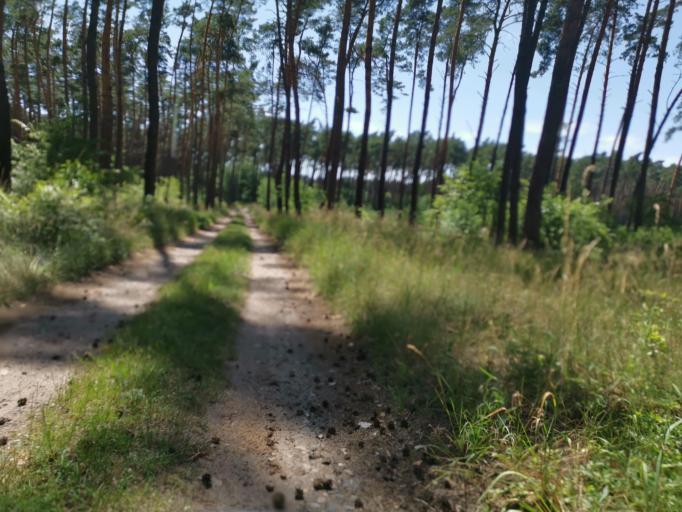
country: CZ
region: South Moravian
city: Rohatec
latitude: 48.8996
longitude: 17.2076
